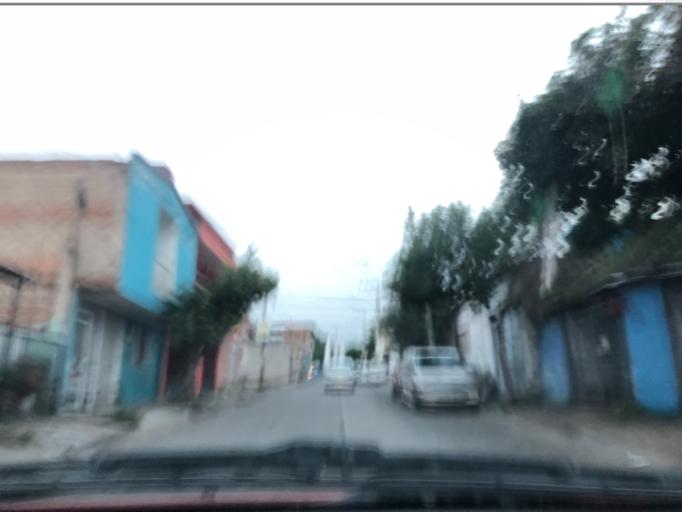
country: MX
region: Jalisco
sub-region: San Pedro Tlaquepaque
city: Paseo del Prado
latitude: 20.6143
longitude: -103.3928
